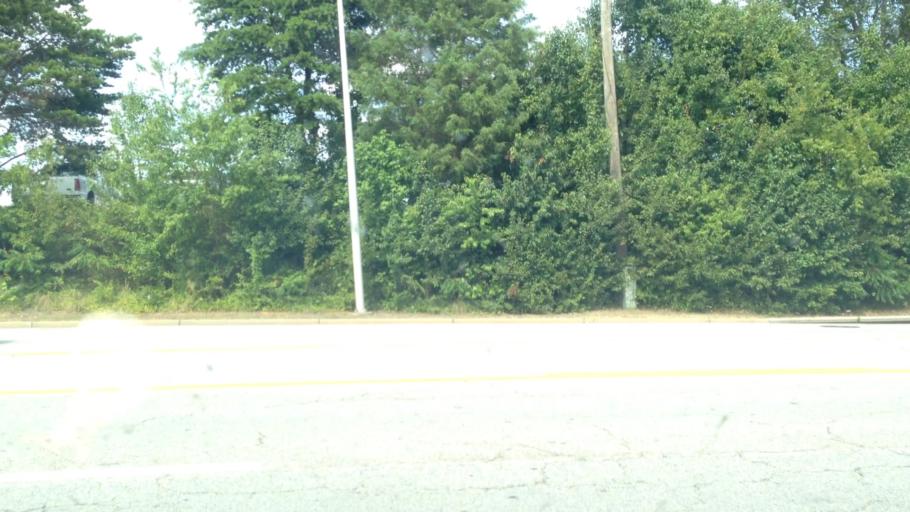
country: US
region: Virginia
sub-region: City of Danville
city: Danville
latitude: 36.5926
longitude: -79.4262
